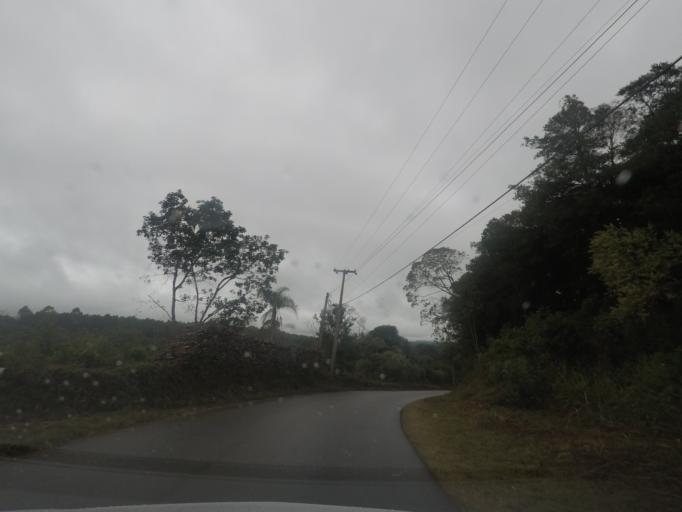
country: BR
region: Parana
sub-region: Campina Grande Do Sul
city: Campina Grande do Sul
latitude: -25.3026
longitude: -49.1287
